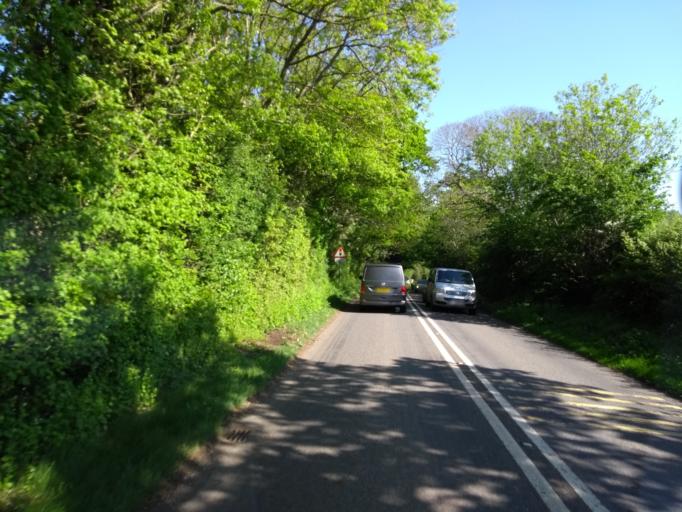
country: GB
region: England
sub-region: Devon
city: Axminster
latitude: 50.7925
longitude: -2.9861
